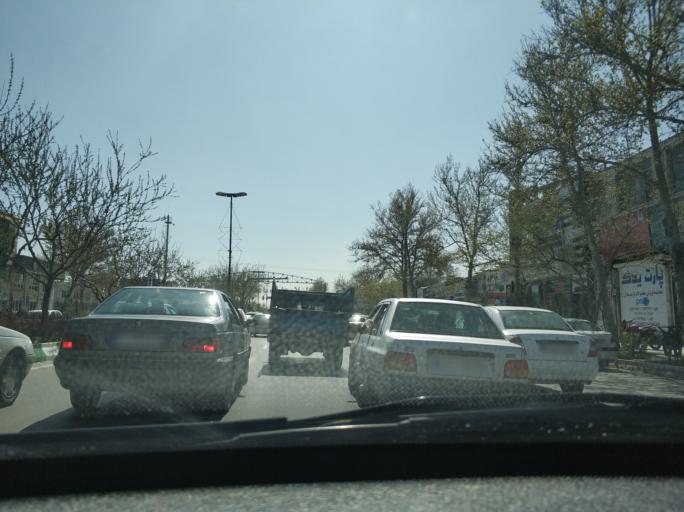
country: IR
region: Razavi Khorasan
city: Mashhad
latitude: 36.2631
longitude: 59.6036
